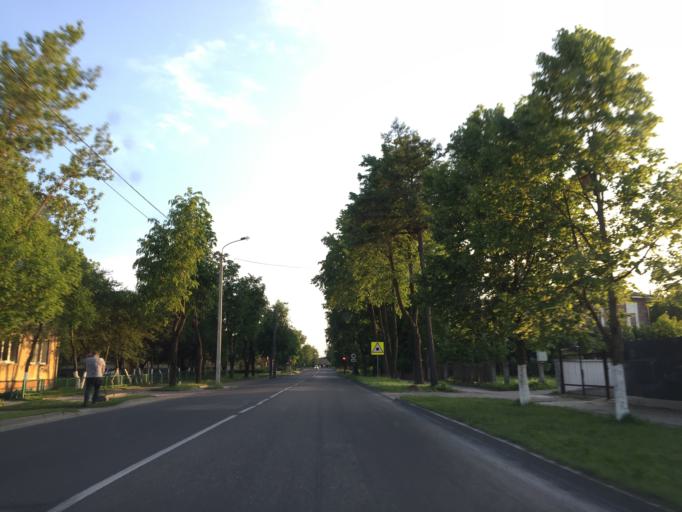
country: LT
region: Siauliu apskritis
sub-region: Siauliai
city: Siauliai
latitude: 55.9413
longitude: 23.3059
